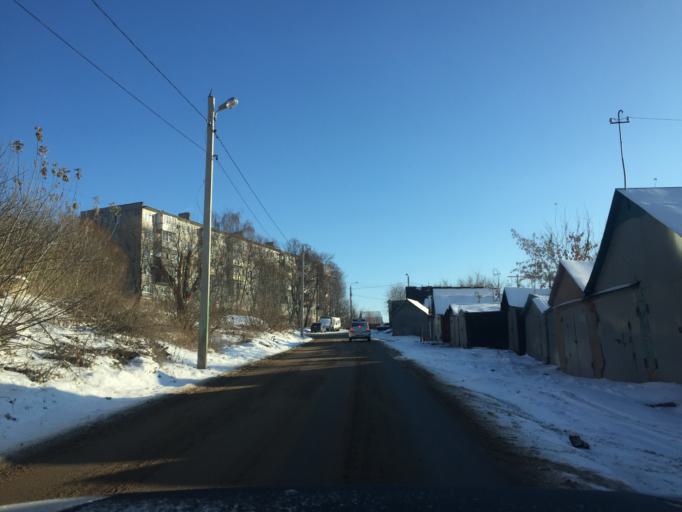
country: RU
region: Tula
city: Tula
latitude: 54.1898
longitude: 37.6824
